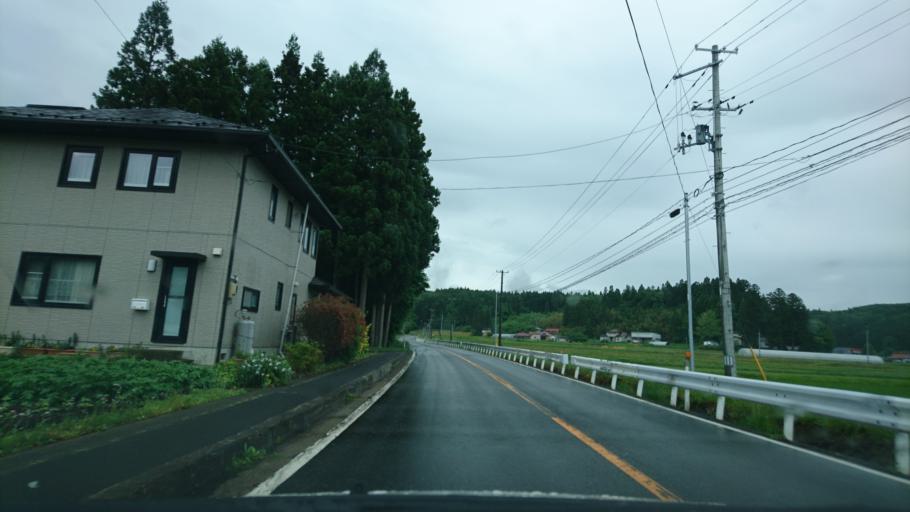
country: JP
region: Iwate
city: Ichinoseki
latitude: 38.9723
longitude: 140.9930
